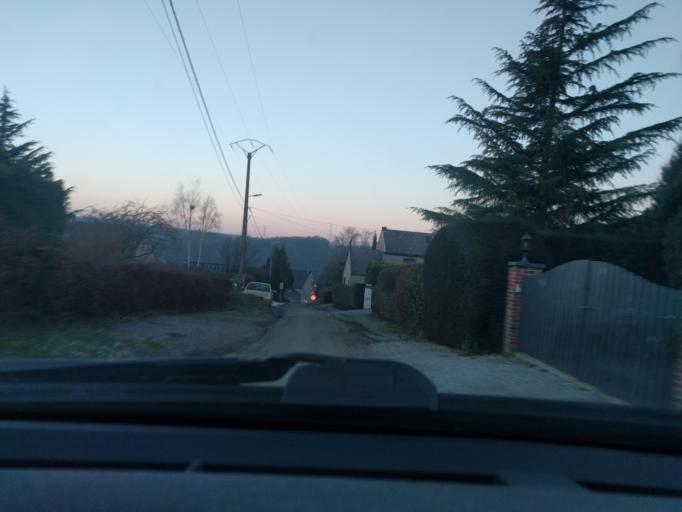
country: BE
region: Wallonia
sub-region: Province de Namur
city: Andenne
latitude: 50.4865
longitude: 5.0336
